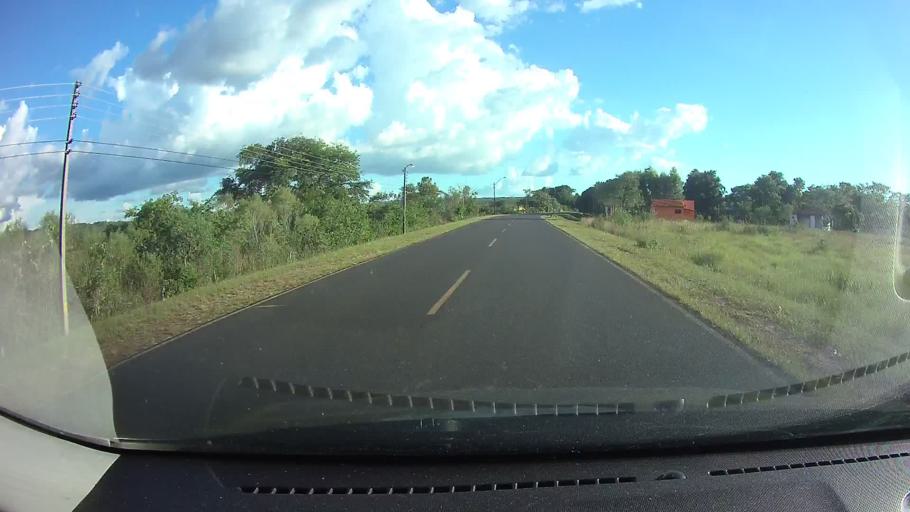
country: PY
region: Cordillera
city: Emboscada
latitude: -25.1516
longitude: -57.2610
